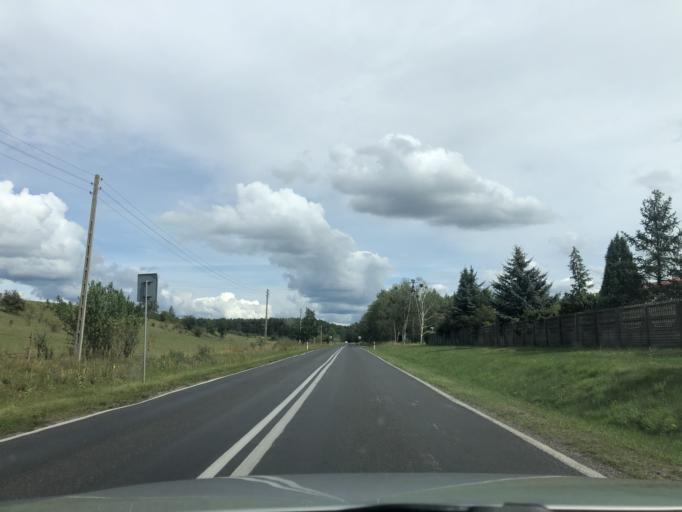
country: PL
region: Greater Poland Voivodeship
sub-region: Powiat pilski
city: Szydlowo
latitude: 53.0981
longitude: 16.6442
